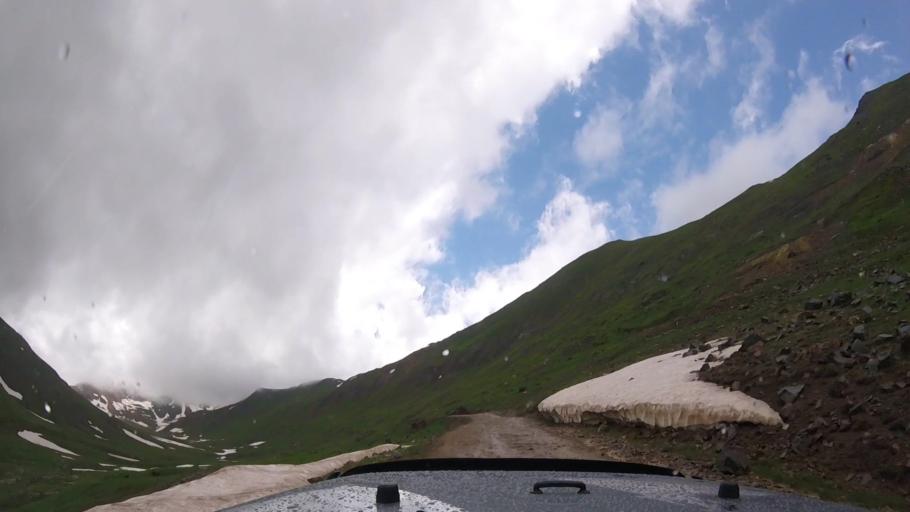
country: US
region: Colorado
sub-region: Ouray County
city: Ouray
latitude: 37.9309
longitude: -107.6035
